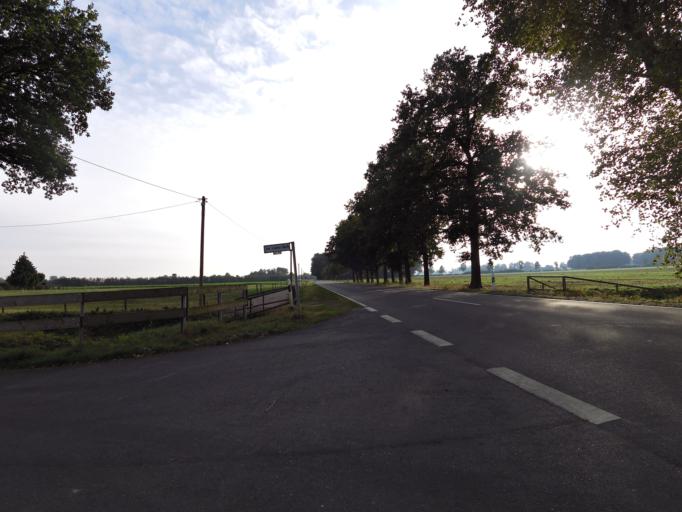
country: DE
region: North Rhine-Westphalia
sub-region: Regierungsbezirk Dusseldorf
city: Bocholt
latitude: 51.8020
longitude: 6.5605
